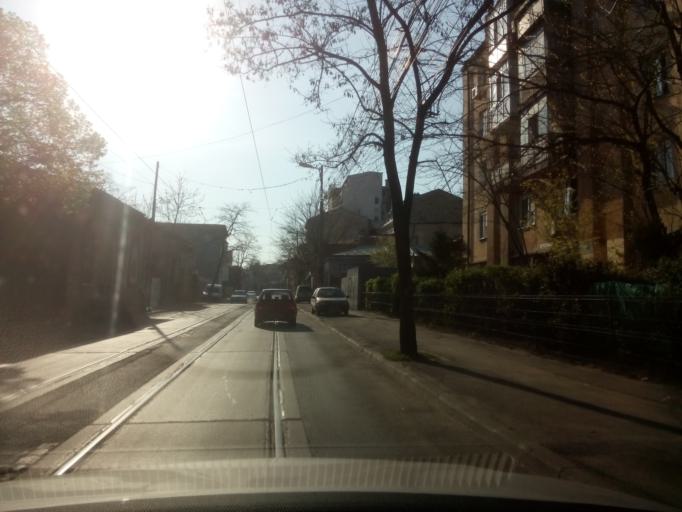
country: RO
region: Bucuresti
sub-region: Municipiul Bucuresti
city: Bucharest
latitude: 44.4332
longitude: 26.1194
